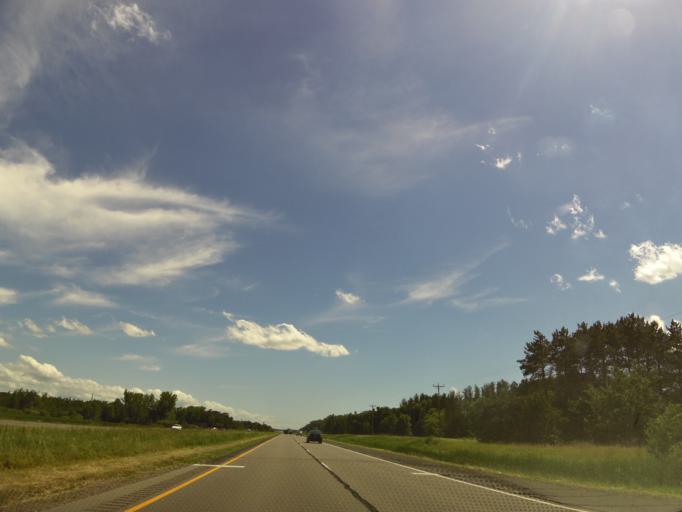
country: US
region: Minnesota
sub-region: Stearns County
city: Sartell
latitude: 45.6808
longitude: -94.1735
